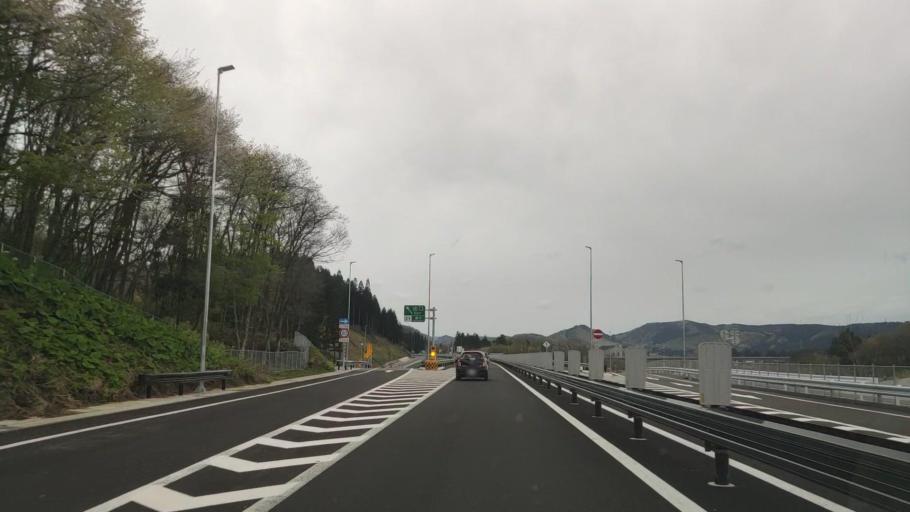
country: JP
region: Akita
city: Takanosu
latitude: 40.2058
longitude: 140.3173
